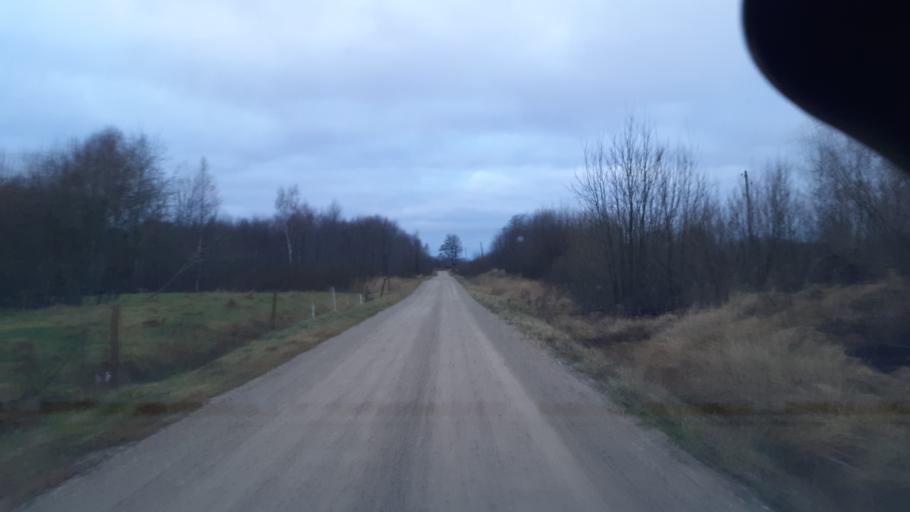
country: LV
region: Alsunga
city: Alsunga
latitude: 56.9046
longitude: 21.6885
